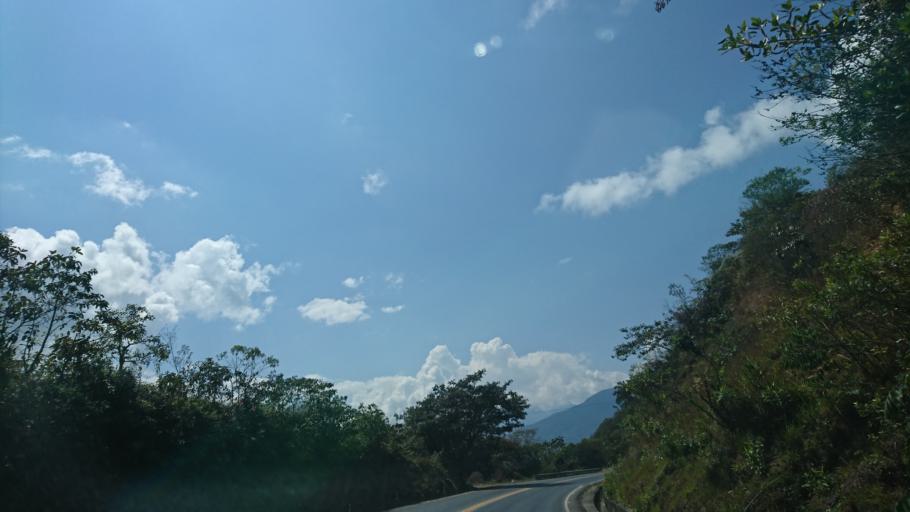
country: BO
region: La Paz
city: Coroico
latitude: -16.2120
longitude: -67.8070
